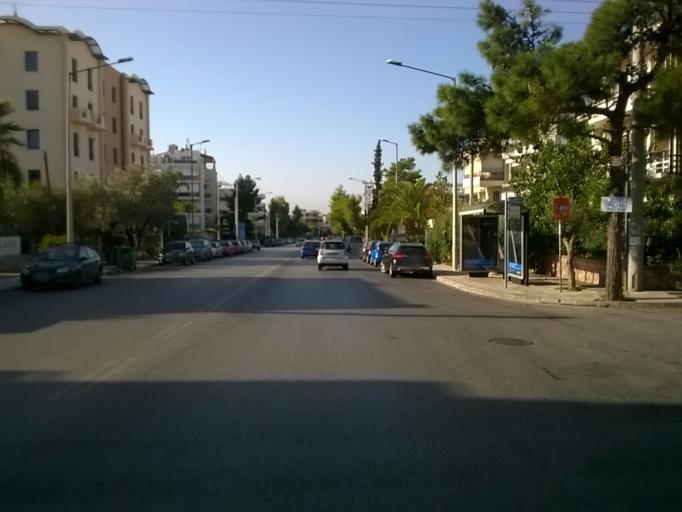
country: GR
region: Attica
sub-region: Nomarchia Athinas
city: Glyfada
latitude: 37.8692
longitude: 23.7582
